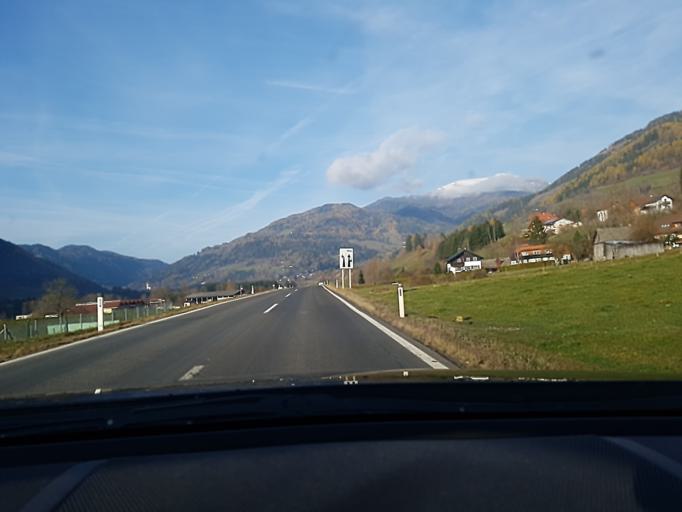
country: AT
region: Styria
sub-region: Politischer Bezirk Murau
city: Sankt Peter am Kammersberg
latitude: 47.1880
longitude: 14.1614
